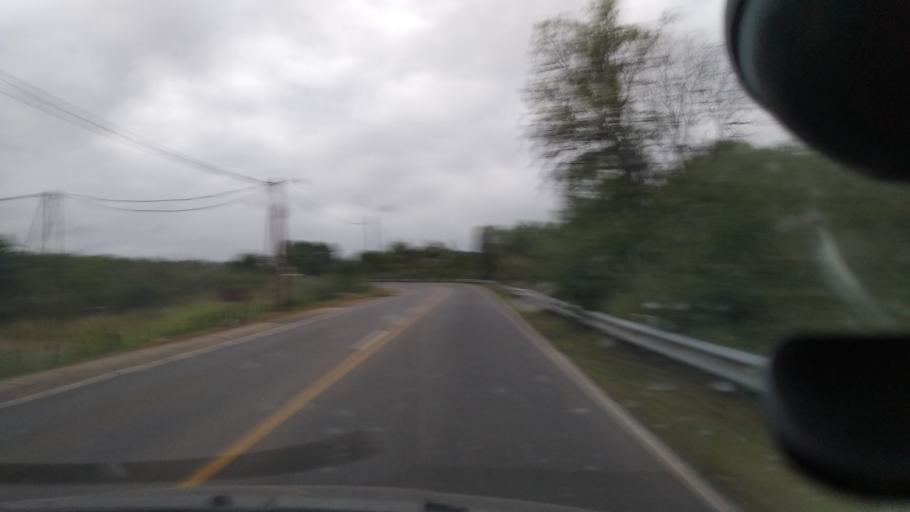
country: AR
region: Cordoba
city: Villa Las Rosas
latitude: -31.9297
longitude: -65.0372
